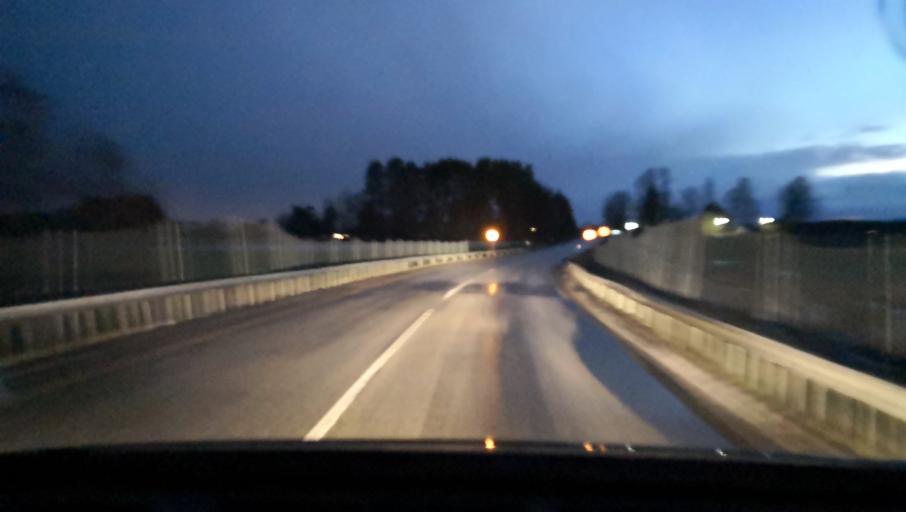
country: SE
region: Vaestmanland
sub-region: Vasteras
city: Skultuna
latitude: 59.7774
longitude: 16.4626
